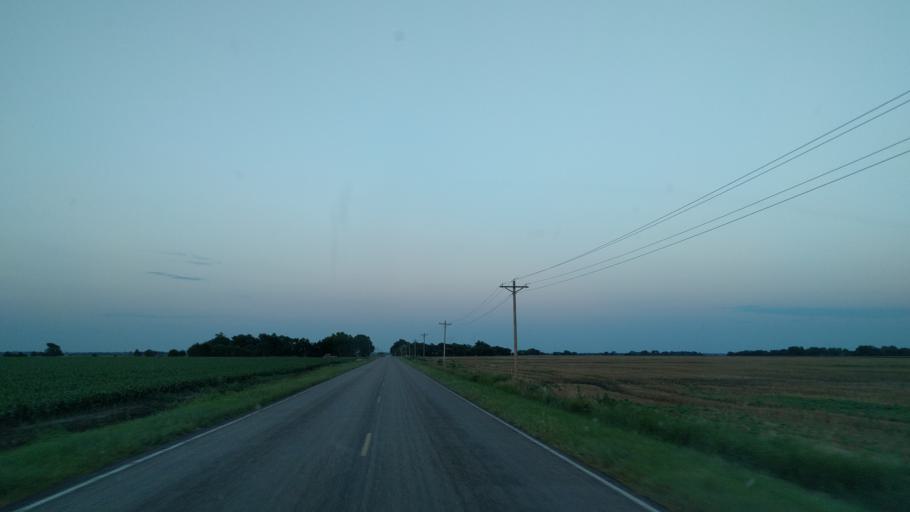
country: US
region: Kansas
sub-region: Rice County
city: Sterling
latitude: 38.2174
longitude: -98.1370
